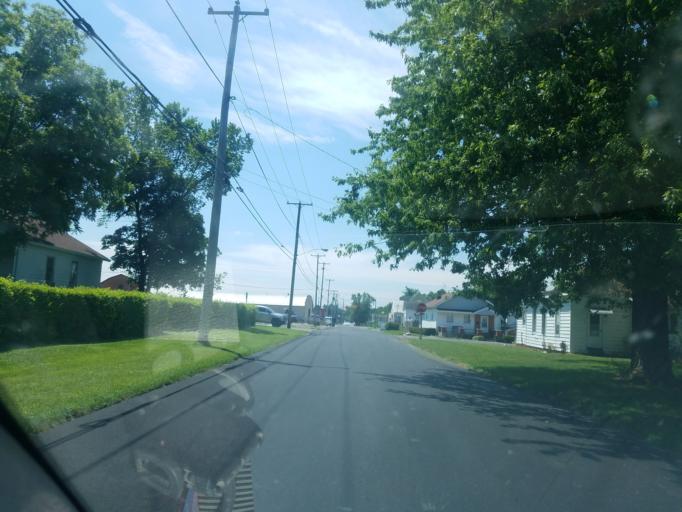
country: US
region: Ohio
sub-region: Hardin County
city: Kenton
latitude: 40.6488
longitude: -83.6134
